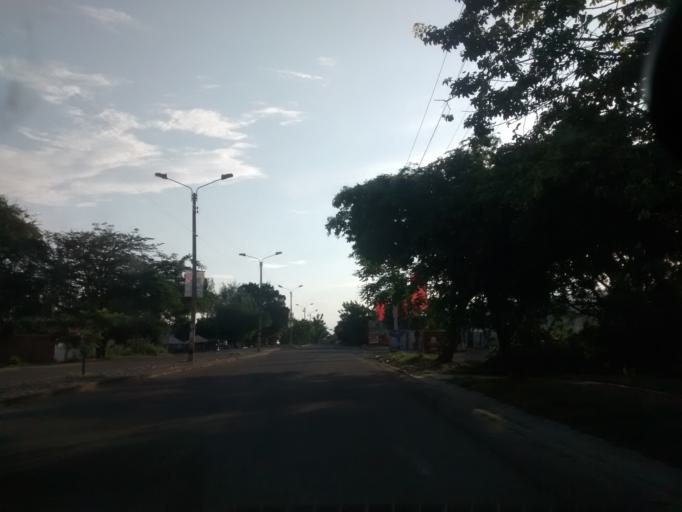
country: CO
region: Tolima
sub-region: Flandes
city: Flandes
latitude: 4.2973
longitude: -74.8217
